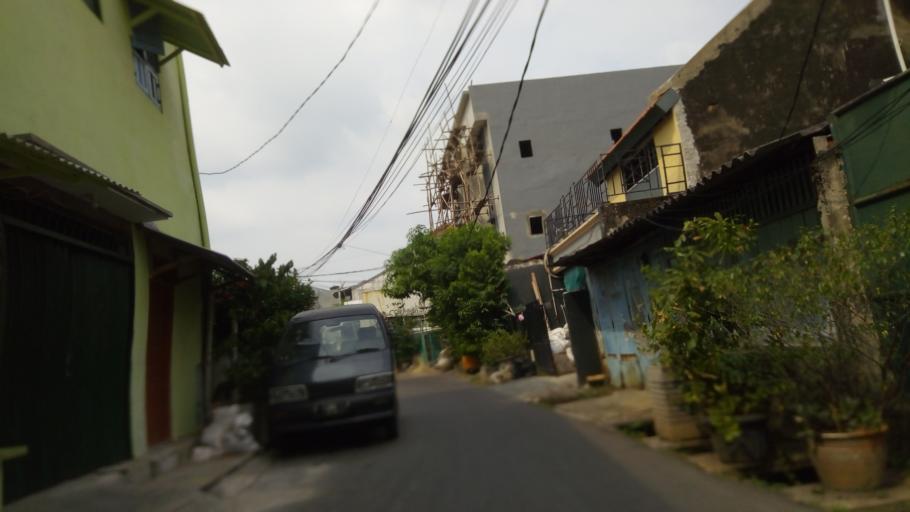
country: ID
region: Jakarta Raya
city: Jakarta
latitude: -6.1561
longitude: 106.8333
